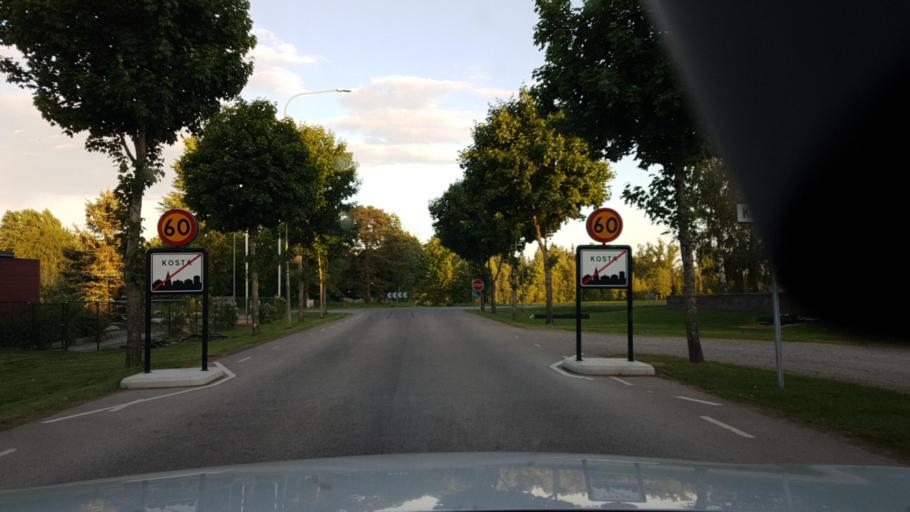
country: SE
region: Kronoberg
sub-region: Lessebo Kommun
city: Lessebo
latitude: 56.8335
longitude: 15.3999
